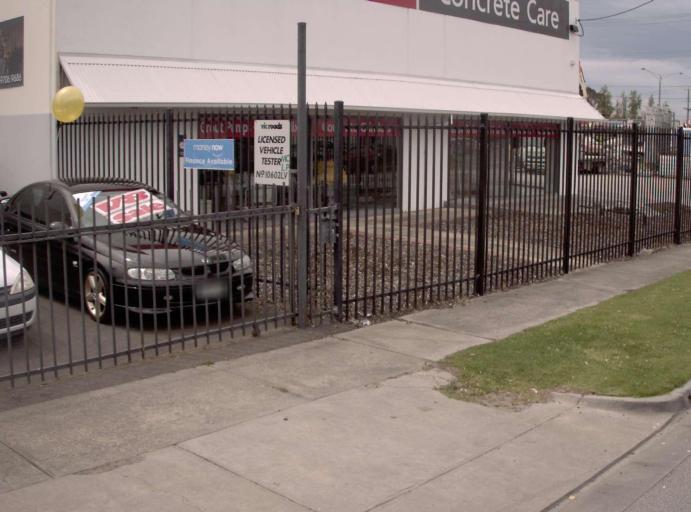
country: AU
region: Victoria
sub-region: Casey
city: Doveton
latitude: -37.9989
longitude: 145.2242
